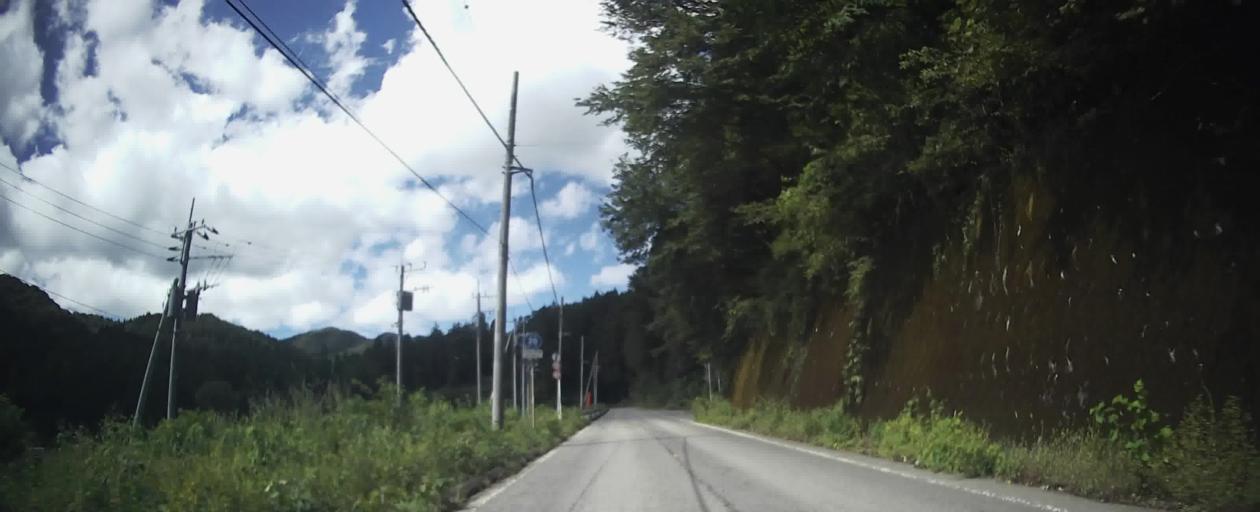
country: JP
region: Gunma
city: Kanekomachi
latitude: 36.4383
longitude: 138.9153
